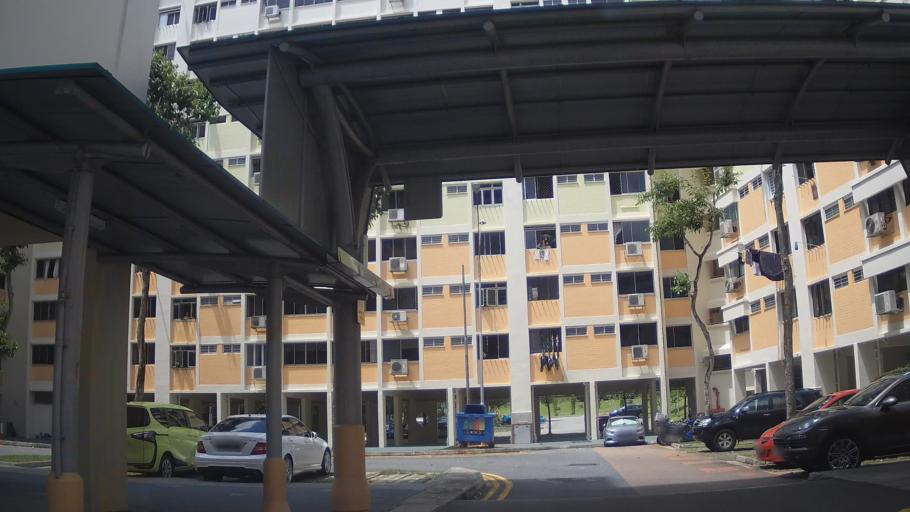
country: MY
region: Johor
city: Johor Bahru
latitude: 1.3770
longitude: 103.7755
